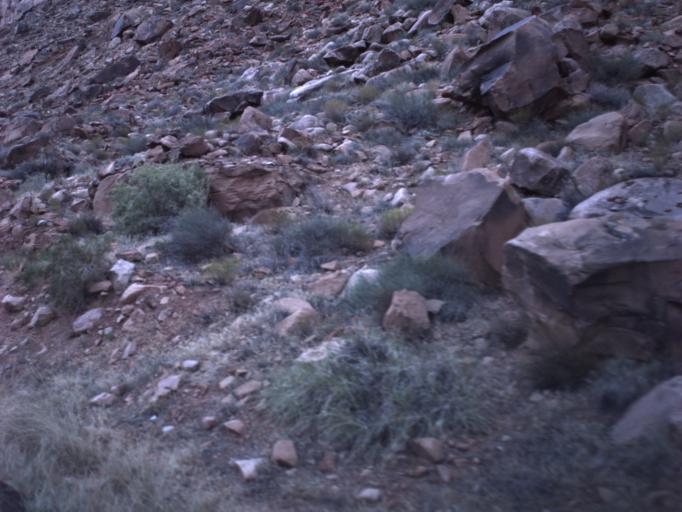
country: US
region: Utah
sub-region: Grand County
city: Moab
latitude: 38.7900
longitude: -109.3347
